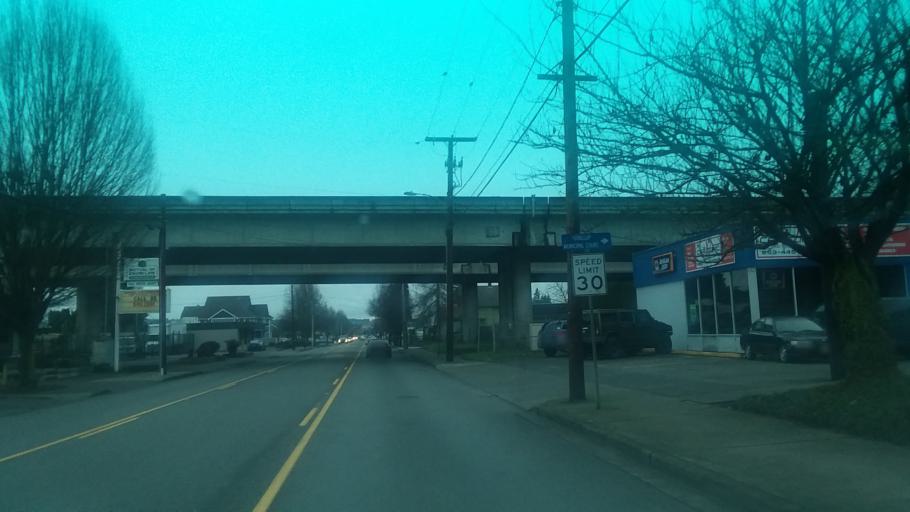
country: US
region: Washington
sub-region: Pierce County
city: Puyallup
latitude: 47.1919
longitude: -122.2818
